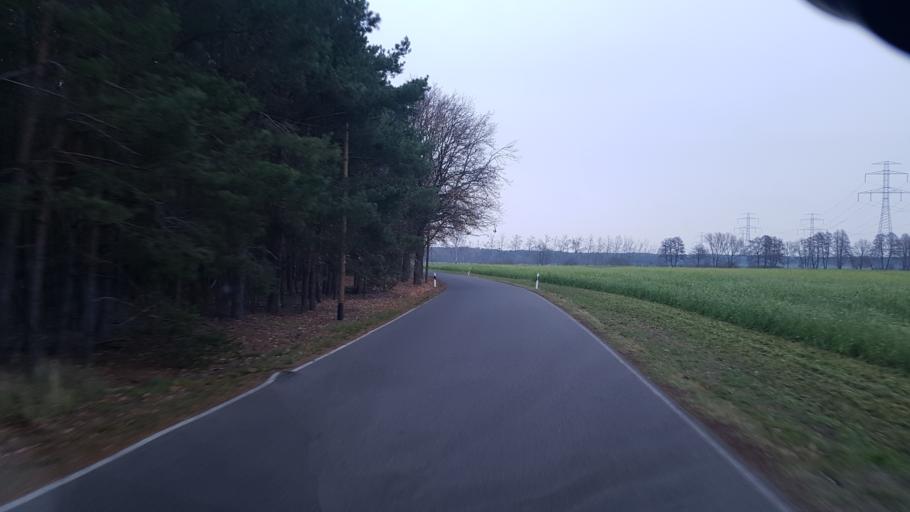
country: DE
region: Brandenburg
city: Peitz
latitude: 51.8830
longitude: 14.4003
